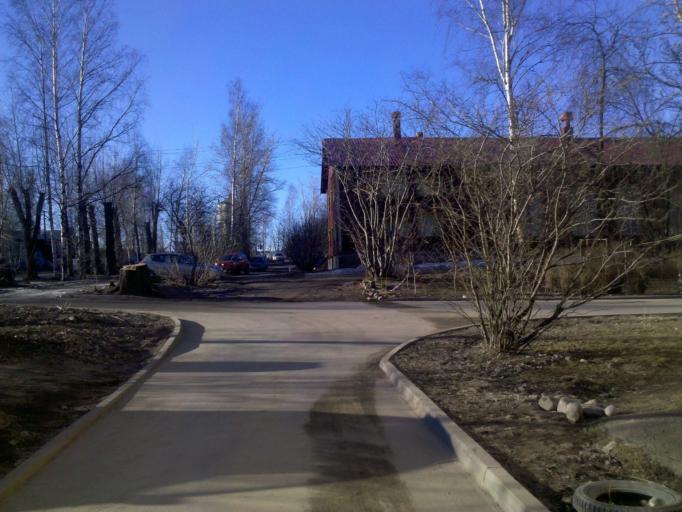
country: RU
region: Republic of Karelia
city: Petrozavodsk
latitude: 61.7984
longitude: 34.3274
